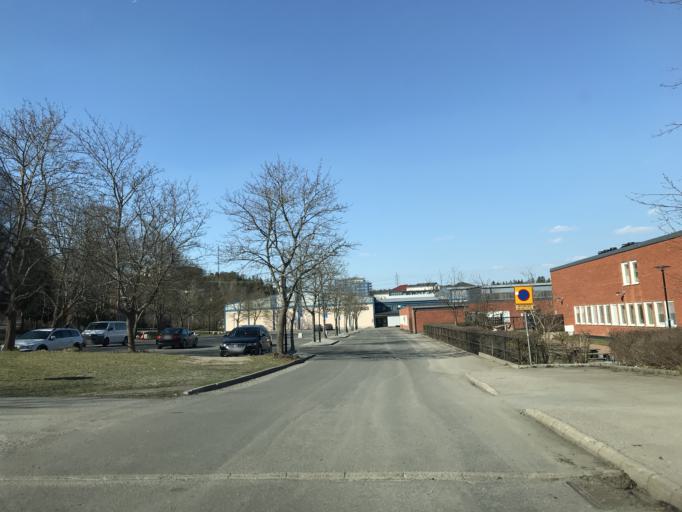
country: SE
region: Stockholm
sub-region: Sollentuna Kommun
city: Sollentuna
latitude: 59.4435
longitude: 17.9514
